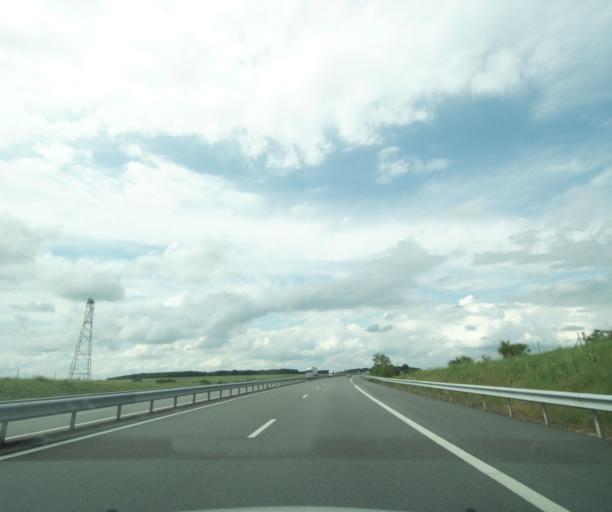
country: FR
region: Centre
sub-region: Departement du Cher
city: Trouy
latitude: 47.0160
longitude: 2.3825
